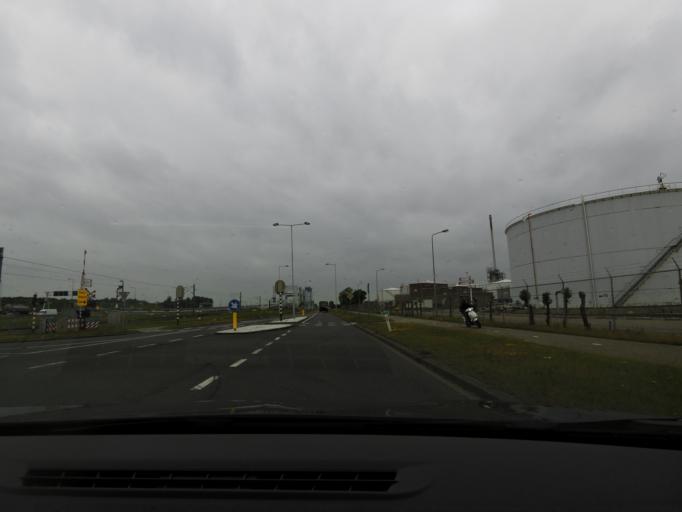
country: NL
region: South Holland
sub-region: Gemeente Spijkenisse
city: Spijkenisse
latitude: 51.8751
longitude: 4.3434
